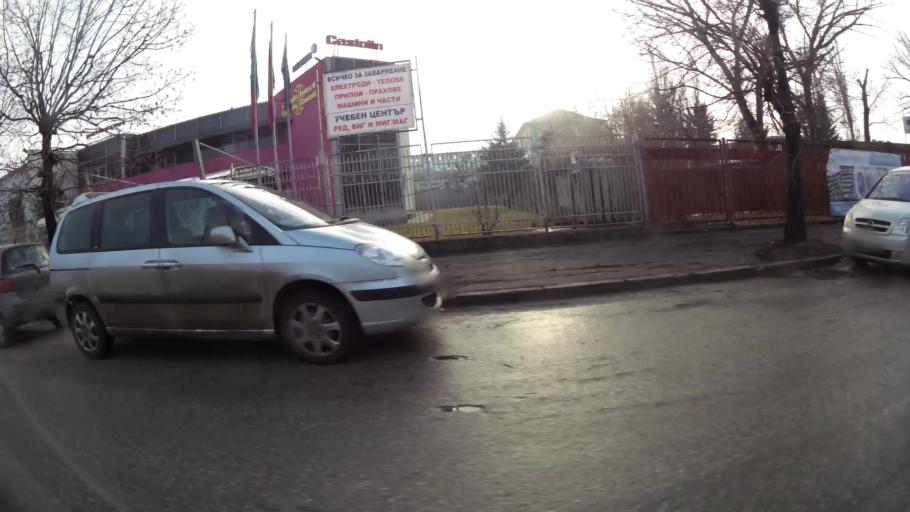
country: BG
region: Sofia-Capital
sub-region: Stolichna Obshtina
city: Sofia
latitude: 42.7345
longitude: 23.3235
